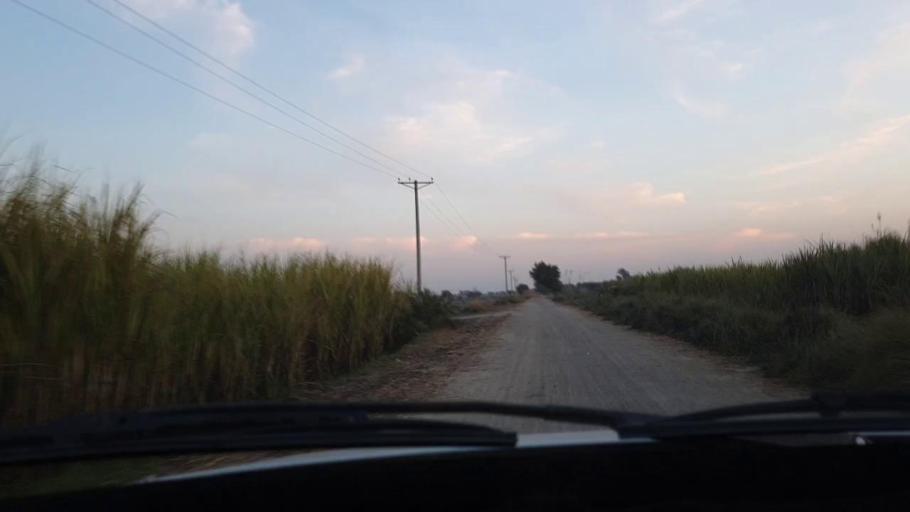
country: PK
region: Sindh
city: Tando Muhammad Khan
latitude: 25.0841
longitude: 68.3976
